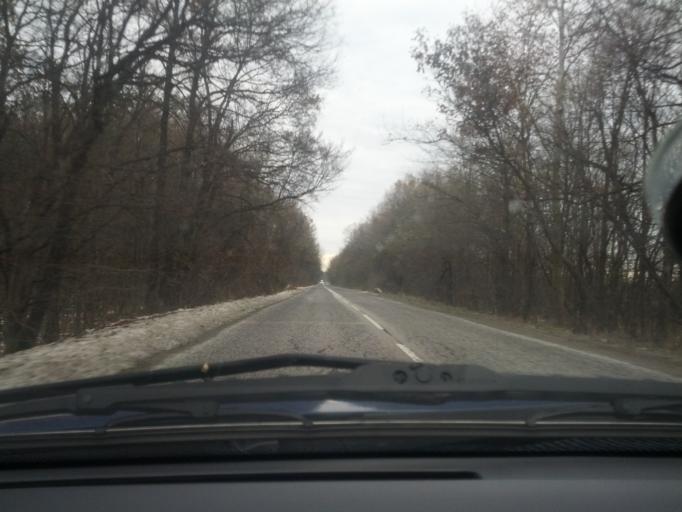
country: BG
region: Vratsa
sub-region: Obshtina Vratsa
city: Vratsa
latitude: 43.2792
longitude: 23.6256
